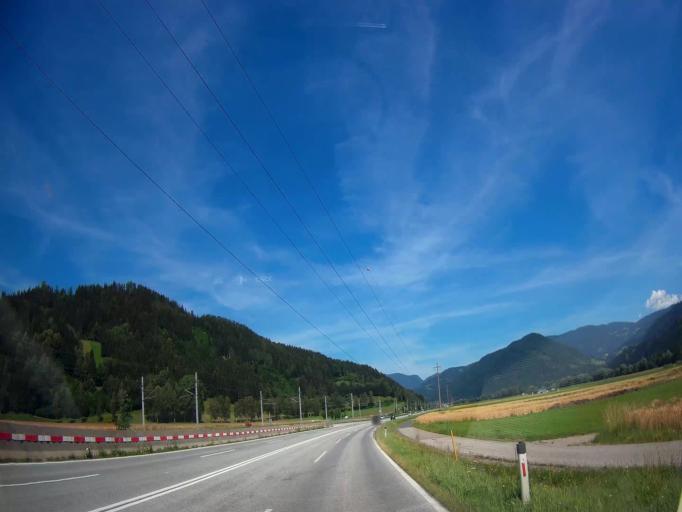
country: AT
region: Carinthia
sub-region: Politischer Bezirk Sankt Veit an der Glan
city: Micheldorf
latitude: 46.9208
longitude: 14.4306
